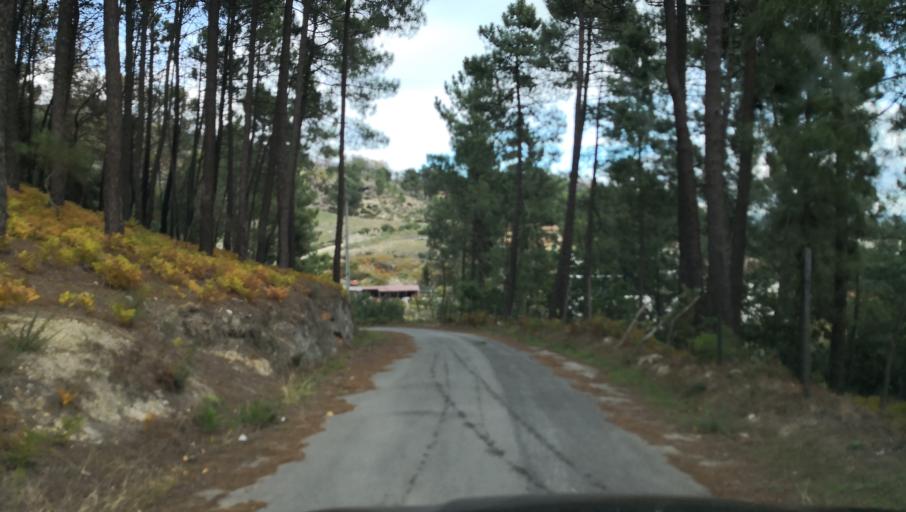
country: PT
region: Vila Real
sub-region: Vila Real
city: Vila Real
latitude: 41.3221
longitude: -7.7672
